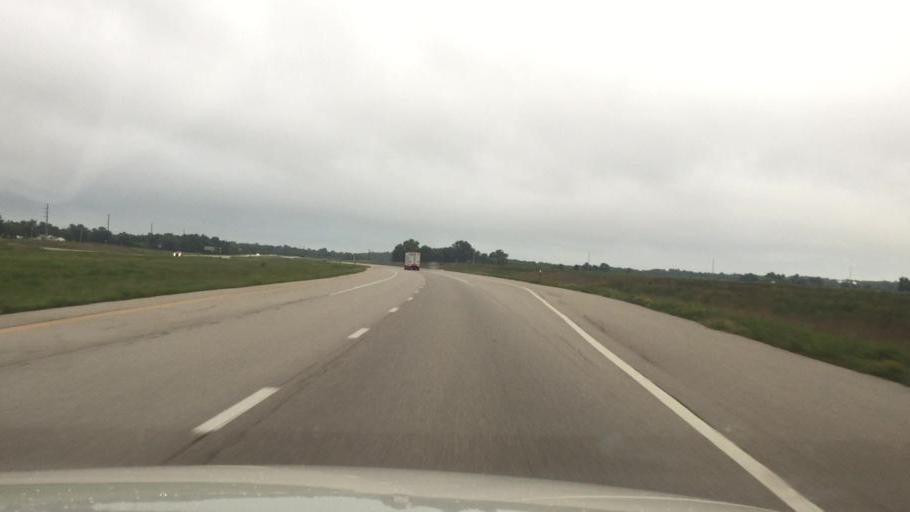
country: US
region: Kansas
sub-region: Montgomery County
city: Coffeyville
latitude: 37.0761
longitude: -95.5893
